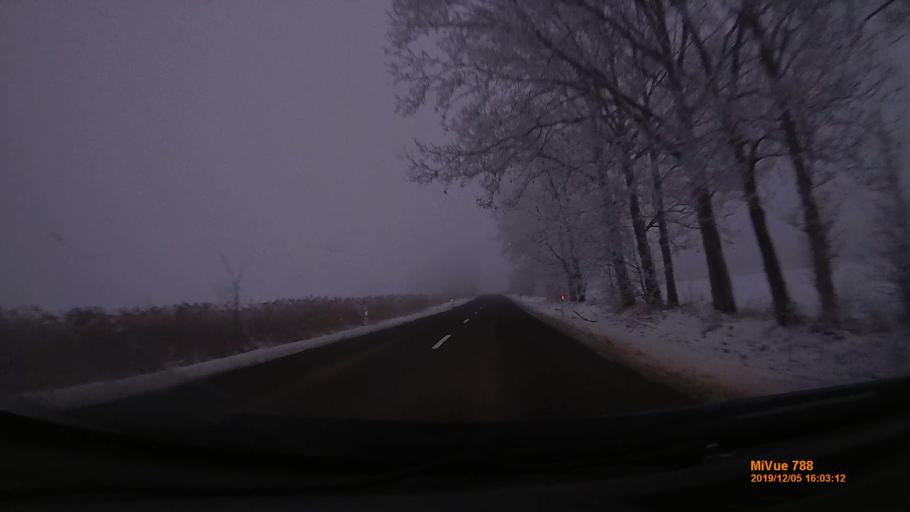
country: HU
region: Borsod-Abauj-Zemplen
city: Tarcal
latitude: 48.1016
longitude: 21.3715
